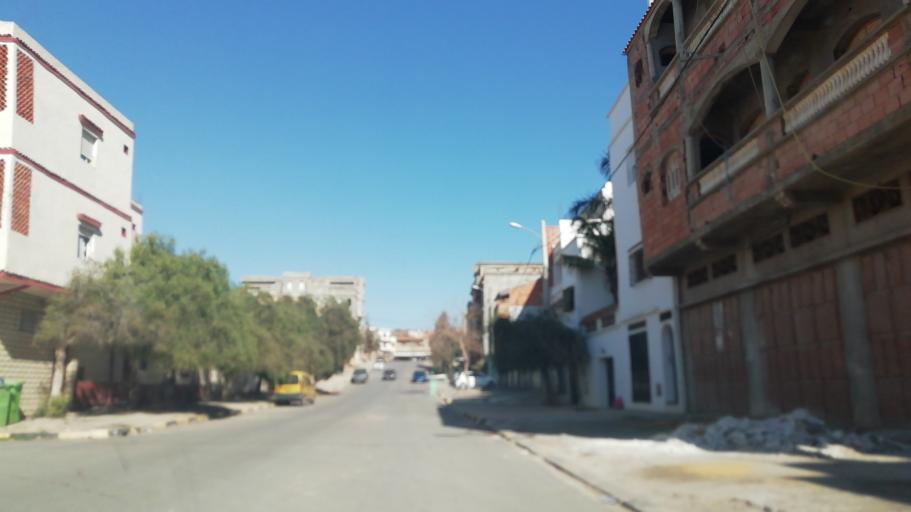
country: DZ
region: Oran
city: Bir el Djir
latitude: 35.7286
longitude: -0.5755
